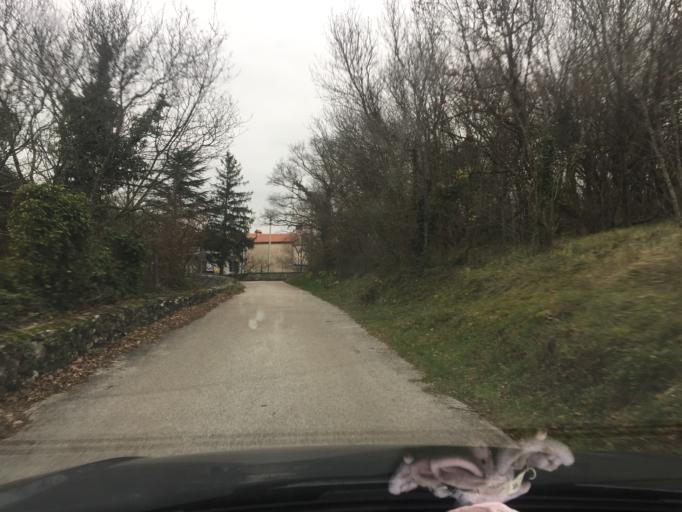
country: IT
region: Friuli Venezia Giulia
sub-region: Provincia di Trieste
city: Zolla
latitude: 45.7204
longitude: 13.8020
